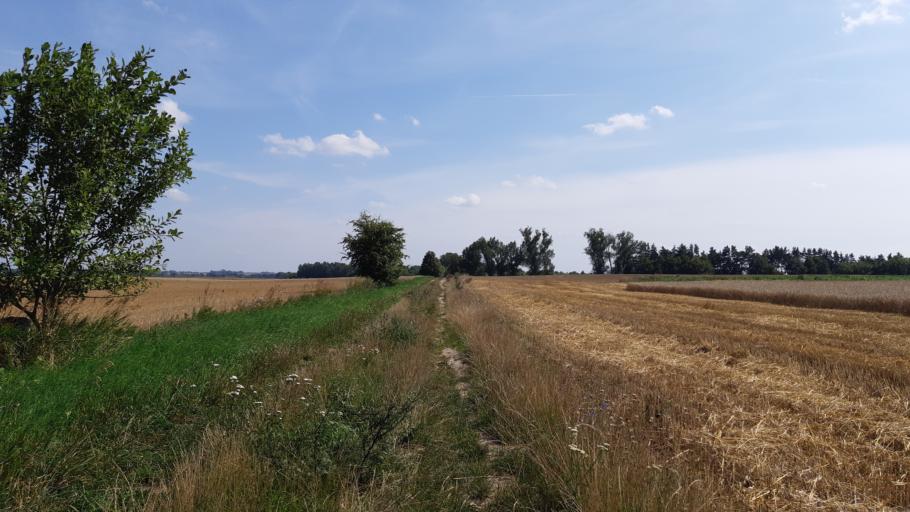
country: LT
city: Virbalis
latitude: 54.6425
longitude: 22.8188
